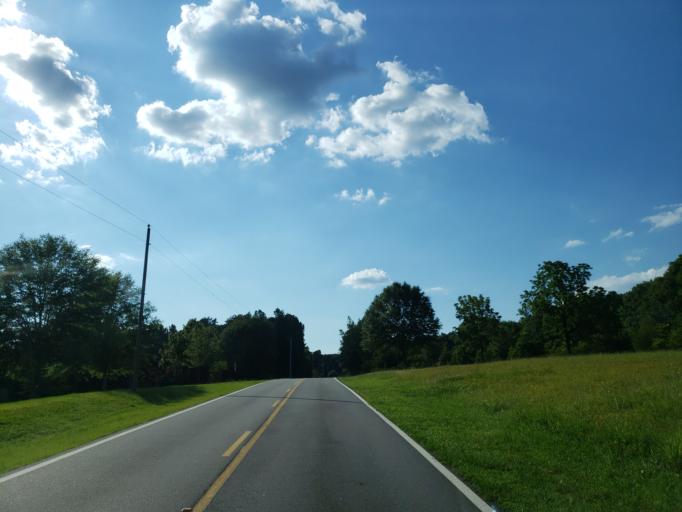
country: US
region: Georgia
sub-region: Haralson County
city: Bremen
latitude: 33.6802
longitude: -85.1271
